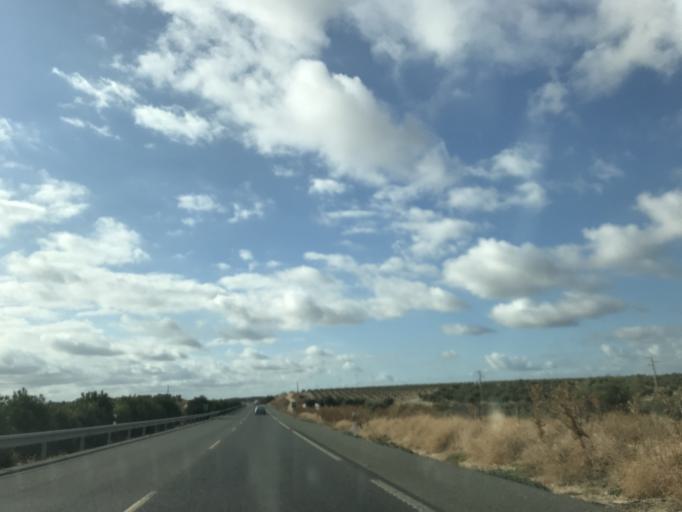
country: ES
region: Andalusia
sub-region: Provincia de Sevilla
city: La Puebla de Cazalla
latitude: 37.2320
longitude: -5.2326
